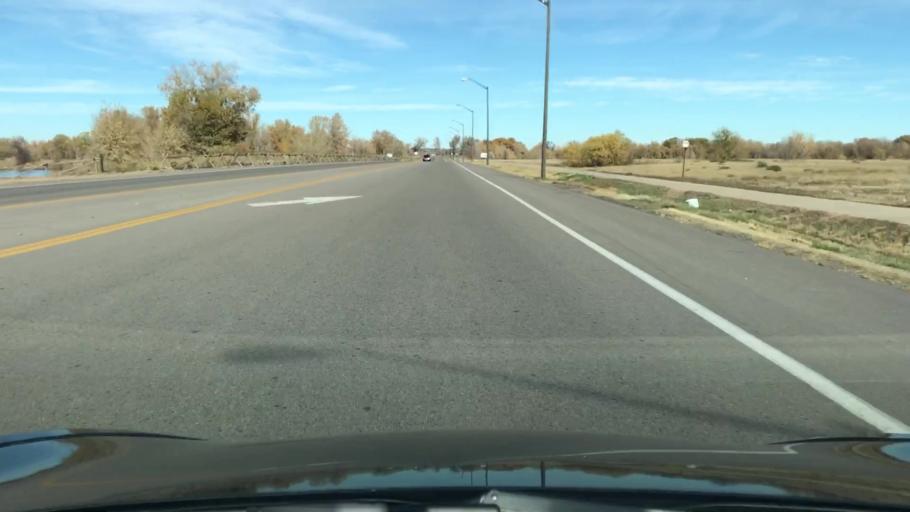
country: US
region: Colorado
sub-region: Larimer County
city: Fort Collins
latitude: 40.5699
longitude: -105.0392
